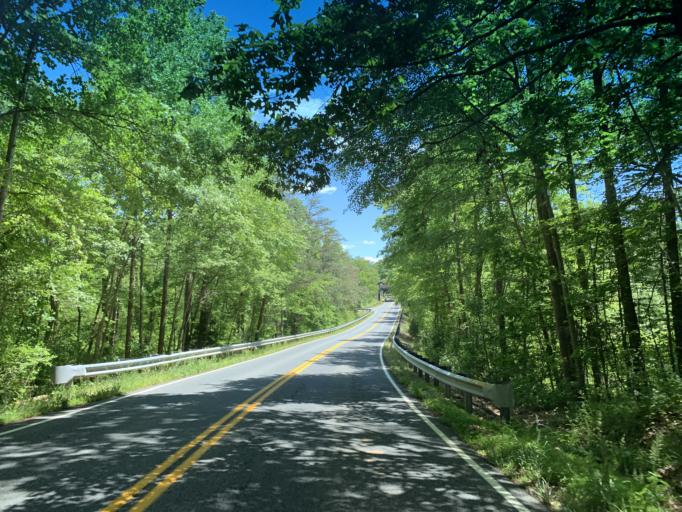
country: US
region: Maryland
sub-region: Cecil County
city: Charlestown
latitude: 39.6226
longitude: -75.9944
